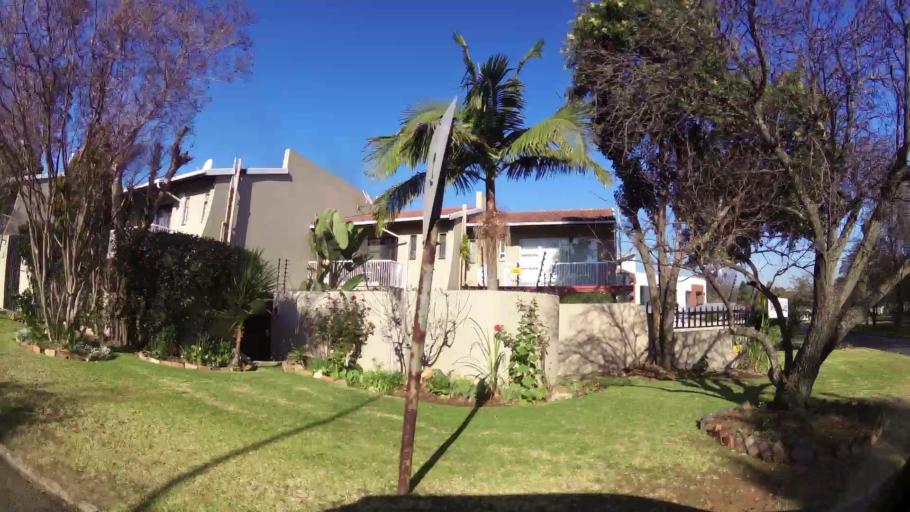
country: ZA
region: Gauteng
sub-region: Ekurhuleni Metropolitan Municipality
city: Germiston
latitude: -26.1860
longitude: 28.1318
